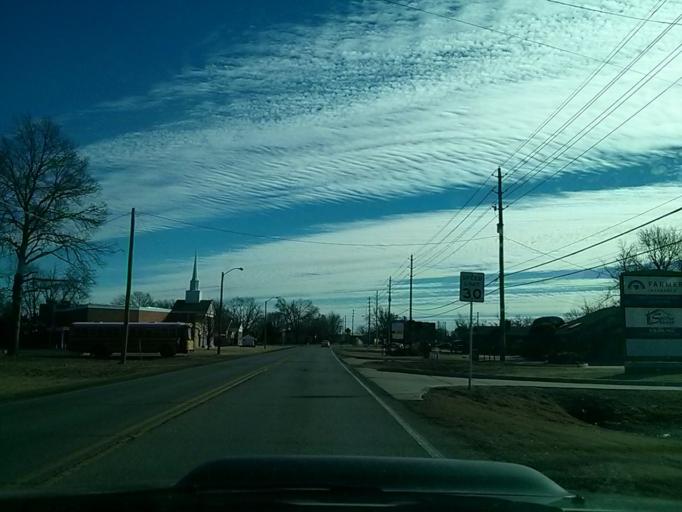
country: US
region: Oklahoma
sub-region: Tulsa County
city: Jenks
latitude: 36.0242
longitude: -95.9844
